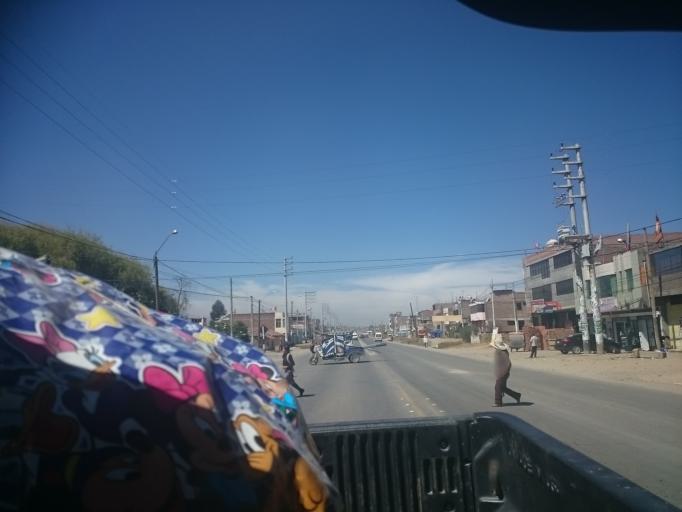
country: PE
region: Junin
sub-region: Provincia de Huancayo
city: San Agustin
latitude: -11.9952
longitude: -75.2552
